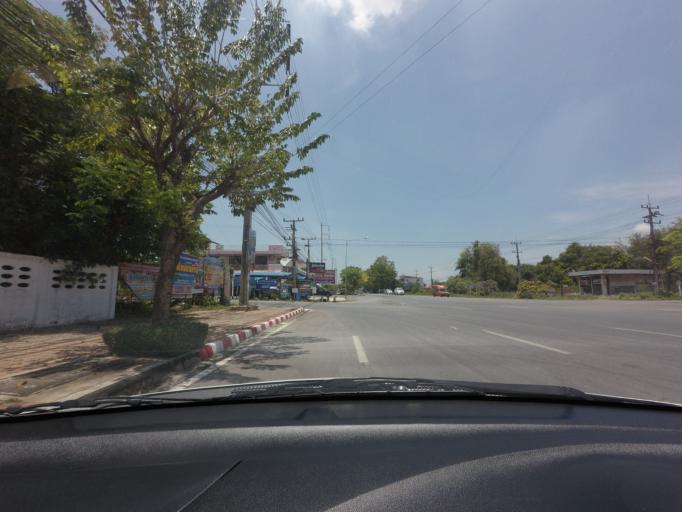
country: TH
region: Suphan Buri
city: Dan Chang
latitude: 14.8410
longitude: 99.7035
